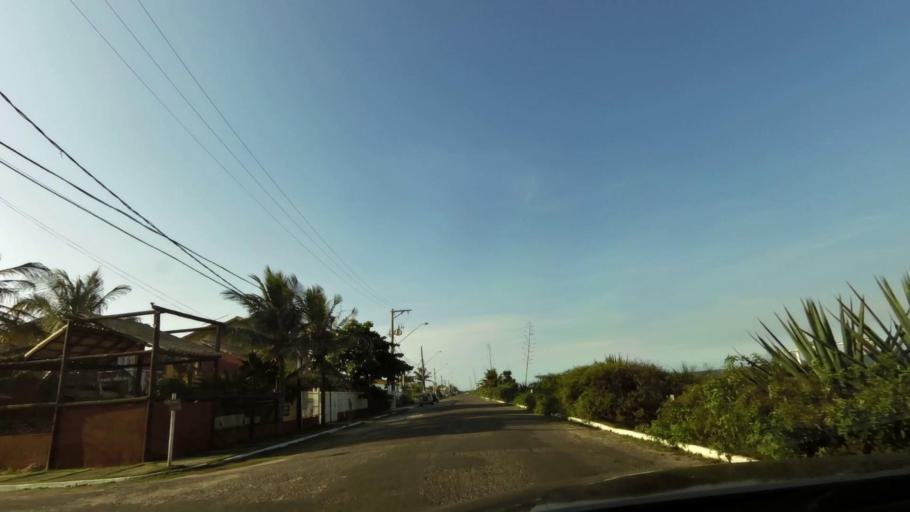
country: BR
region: Espirito Santo
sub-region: Vila Velha
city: Vila Velha
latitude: -20.4758
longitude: -40.3469
